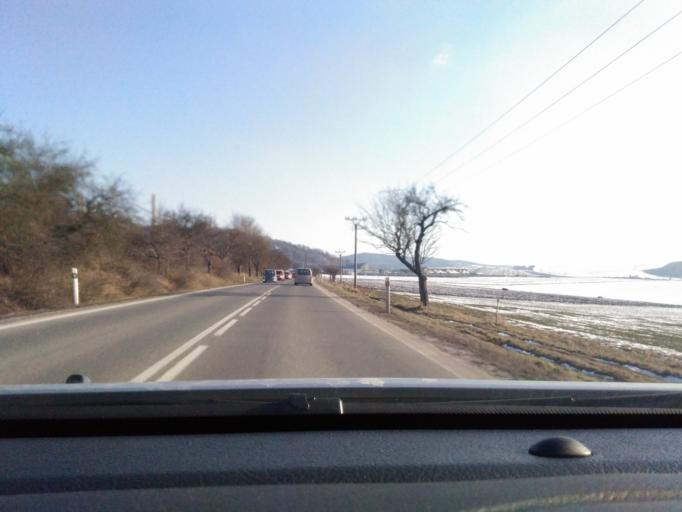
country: CZ
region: South Moravian
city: Kurim
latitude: 49.3037
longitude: 16.5124
